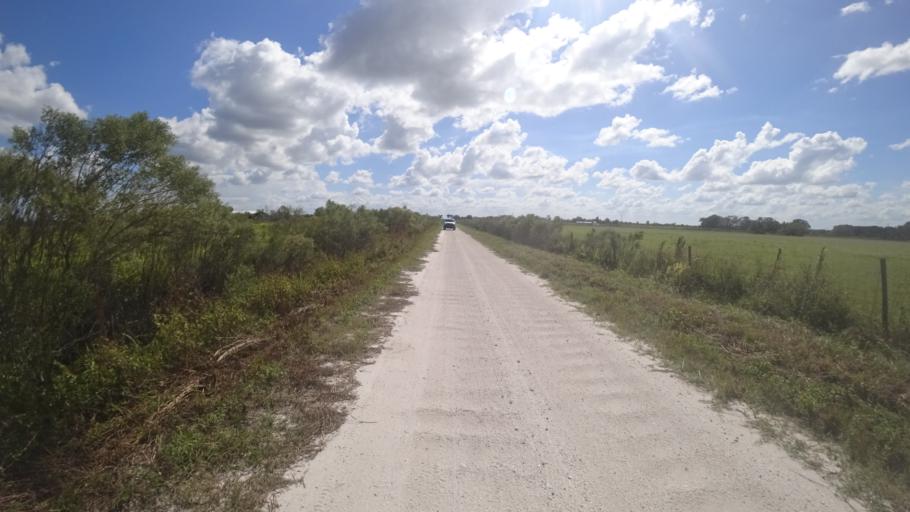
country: US
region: Florida
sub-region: DeSoto County
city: Arcadia
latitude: 27.3159
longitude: -82.1051
